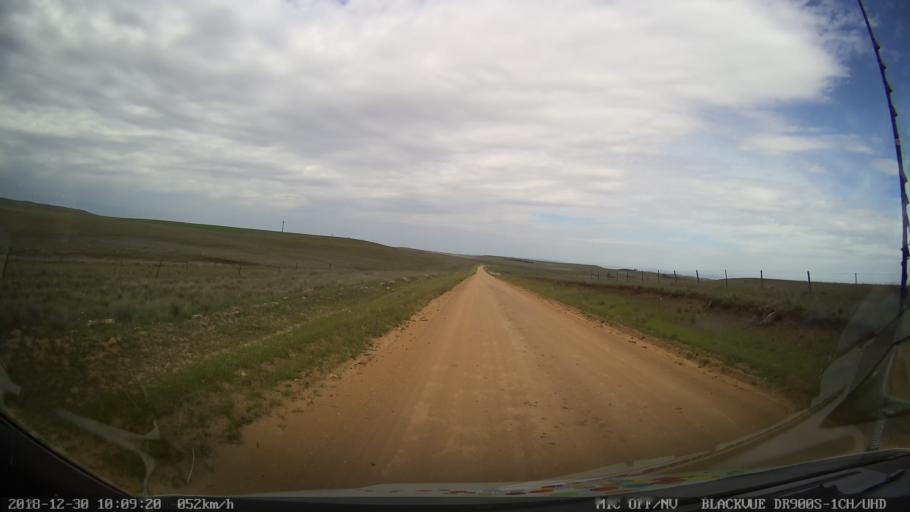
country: AU
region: New South Wales
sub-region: Cooma-Monaro
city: Cooma
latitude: -36.5480
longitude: 149.1064
